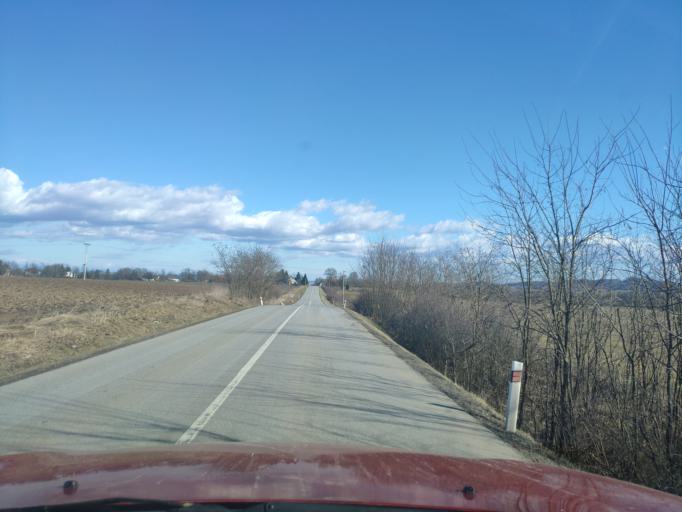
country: HU
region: Borsod-Abauj-Zemplen
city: Ozd
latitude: 48.2987
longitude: 20.1912
